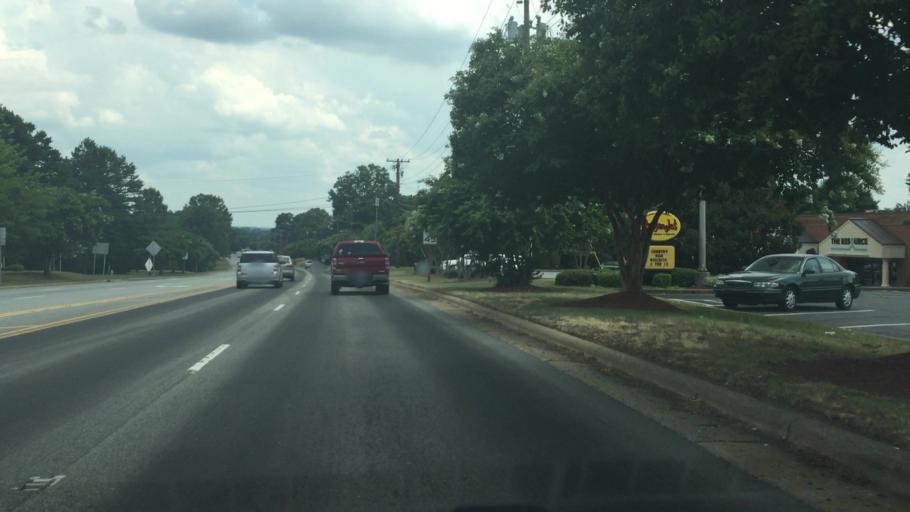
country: US
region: North Carolina
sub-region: Rowan County
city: Franklin
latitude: 35.6921
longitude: -80.5123
